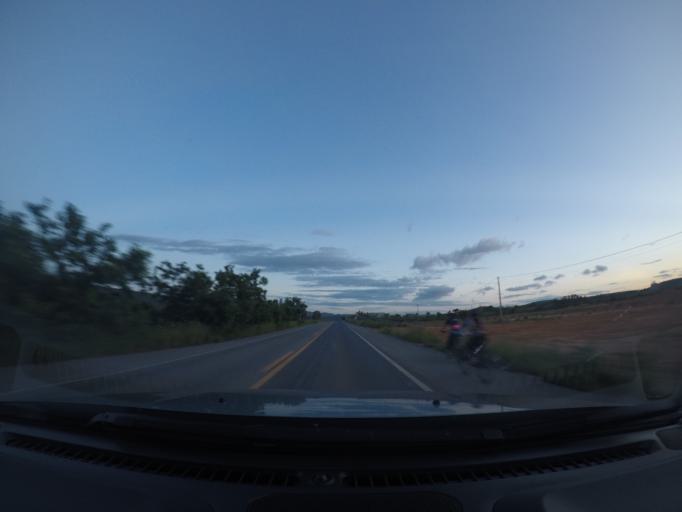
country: BR
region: Bahia
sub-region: Seabra
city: Seabra
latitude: -12.4624
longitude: -41.7469
